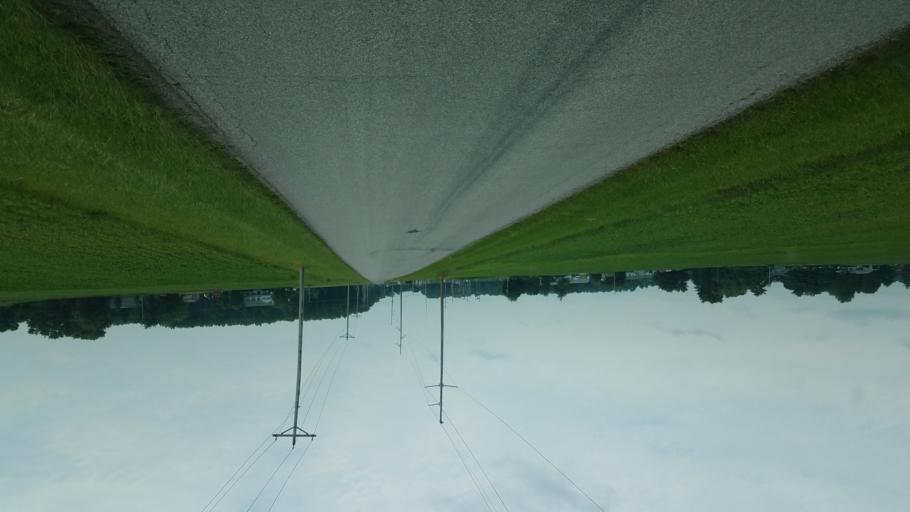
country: US
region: Ohio
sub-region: Delaware County
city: Ashley
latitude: 40.4192
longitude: -82.9095
